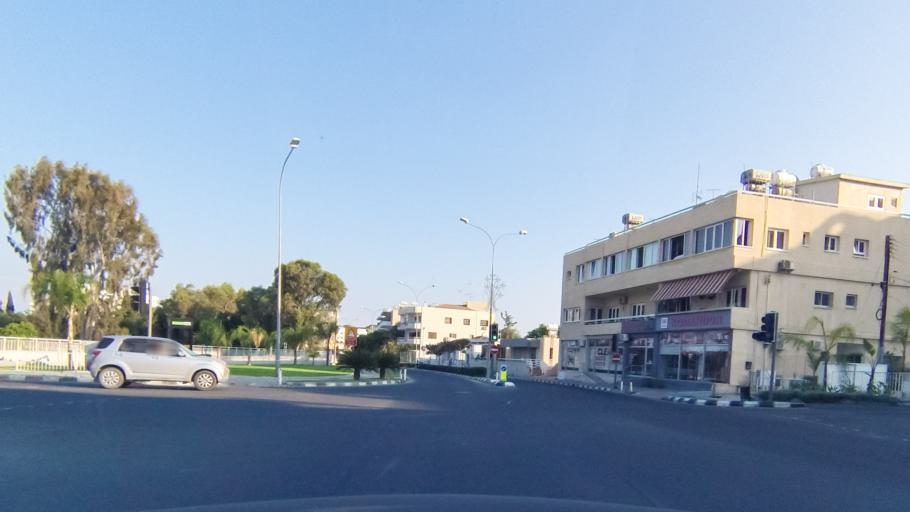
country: CY
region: Limassol
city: Mouttagiaka
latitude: 34.6997
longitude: 33.0880
